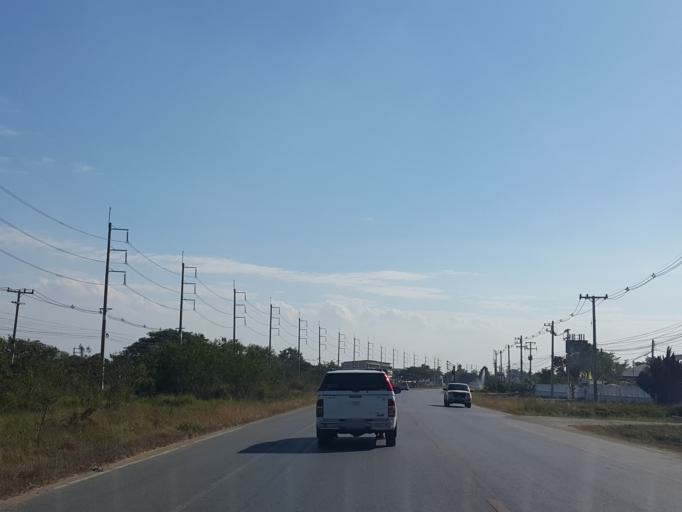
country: TH
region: Chiang Mai
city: San Kamphaeng
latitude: 18.7832
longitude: 99.0700
